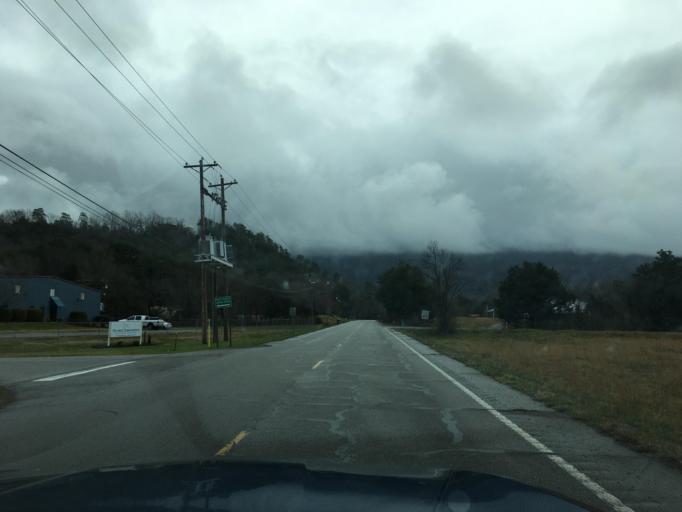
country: US
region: Tennessee
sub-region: Polk County
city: Benton
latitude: 35.1677
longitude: -84.6391
